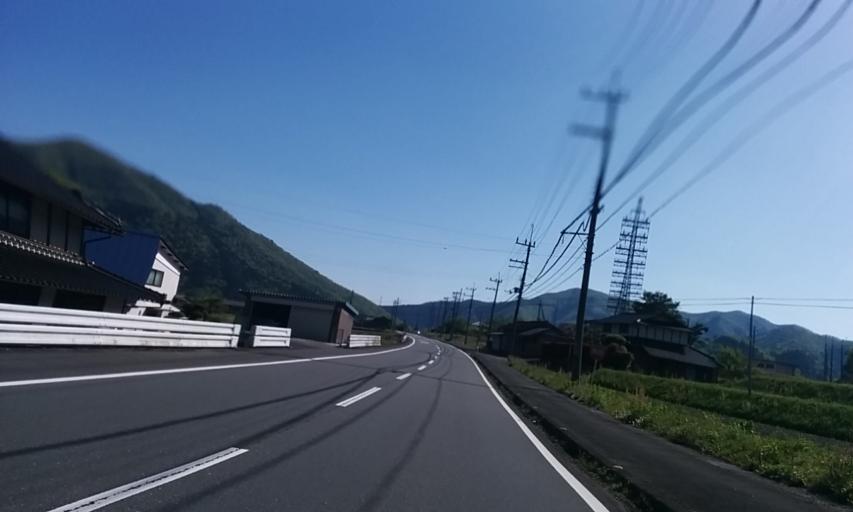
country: JP
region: Kyoto
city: Ayabe
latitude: 35.2545
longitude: 135.4232
